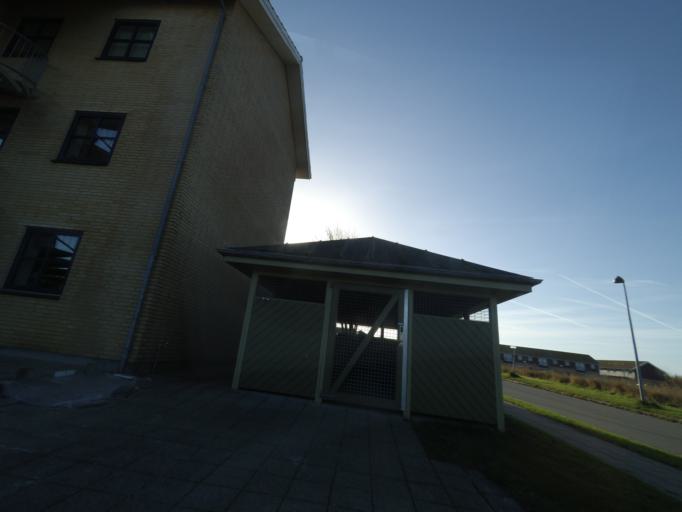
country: DK
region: South Denmark
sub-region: Odense Kommune
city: Hojby
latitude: 55.3271
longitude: 10.4382
